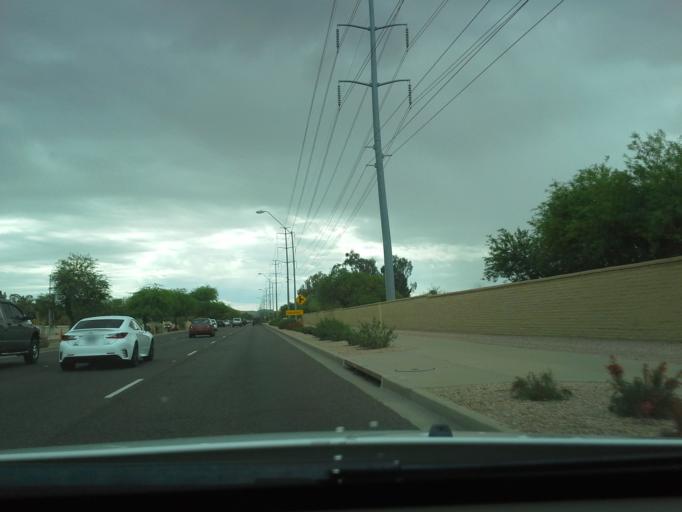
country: US
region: Arizona
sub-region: Maricopa County
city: Scottsdale
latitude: 33.5824
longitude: -111.8630
